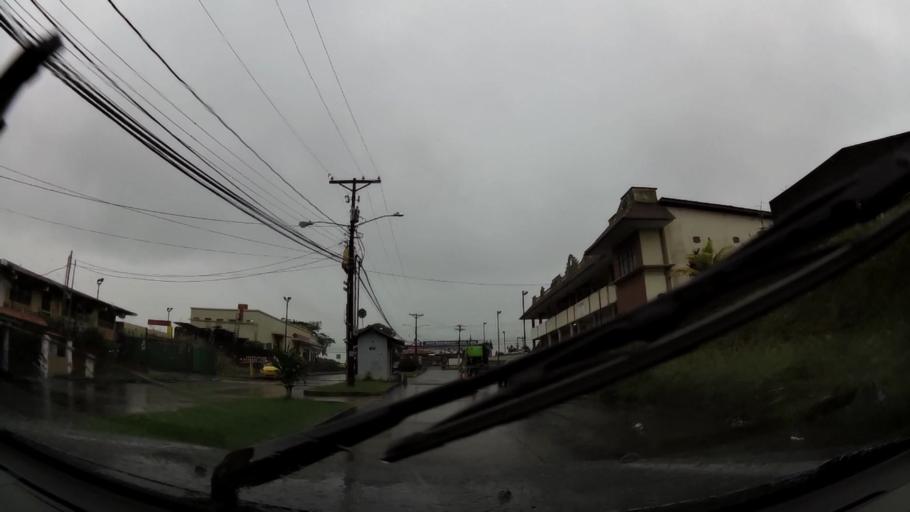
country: PA
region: Colon
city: Sabanitas
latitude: 9.3446
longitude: -79.8065
